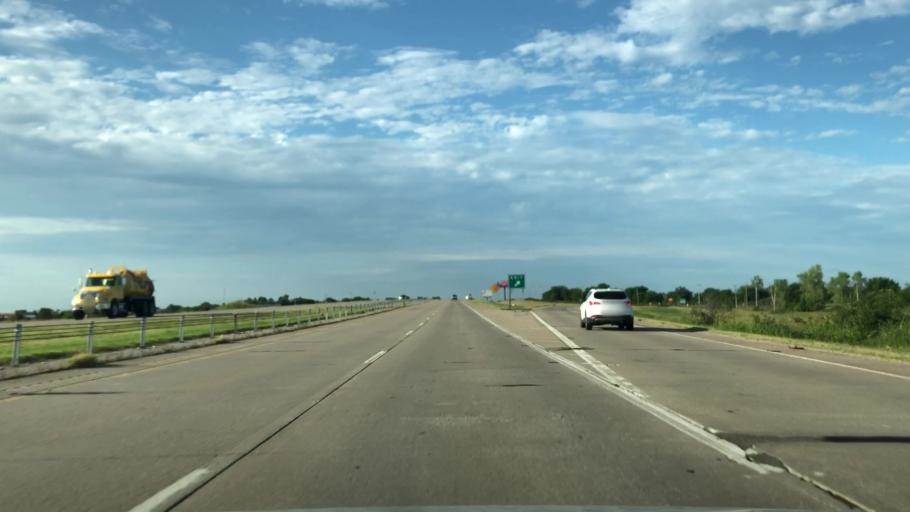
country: US
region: Oklahoma
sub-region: Osage County
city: Skiatook
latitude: 36.3691
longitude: -95.9209
